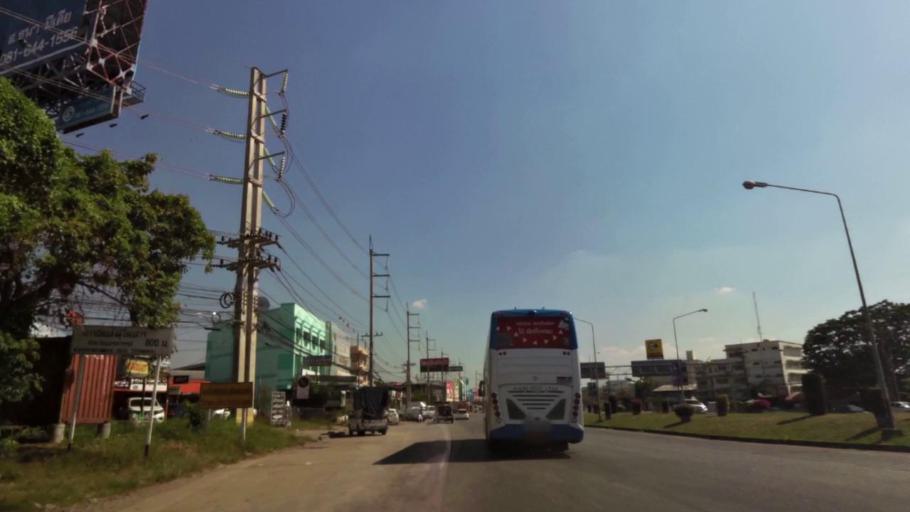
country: TH
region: Nakhon Sawan
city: Nakhon Sawan
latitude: 15.7059
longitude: 100.1126
